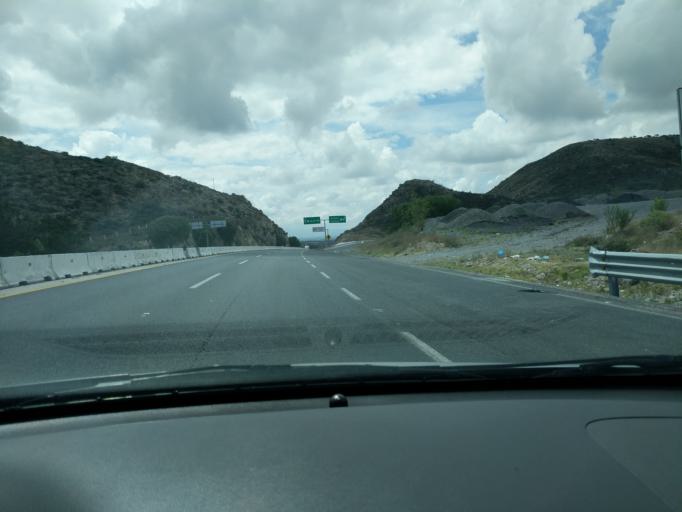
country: MX
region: San Luis Potosi
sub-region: Mexquitic de Carmona
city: Cerrito de Jaral
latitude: 22.2520
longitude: -101.1104
